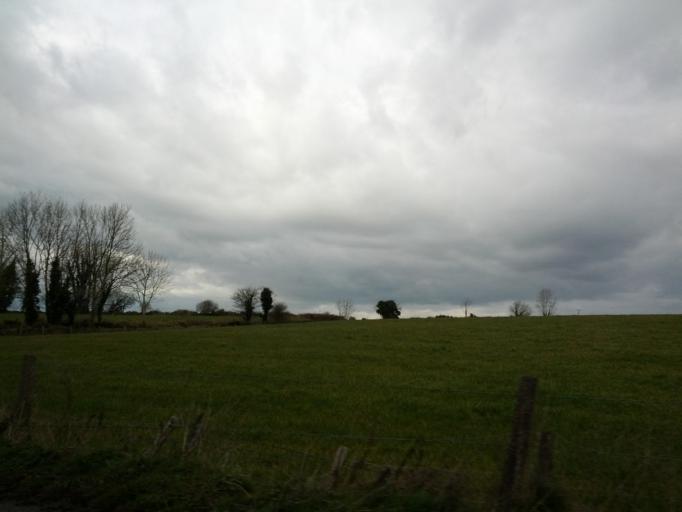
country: IE
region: Connaught
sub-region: County Galway
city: Athenry
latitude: 53.4255
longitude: -8.6376
